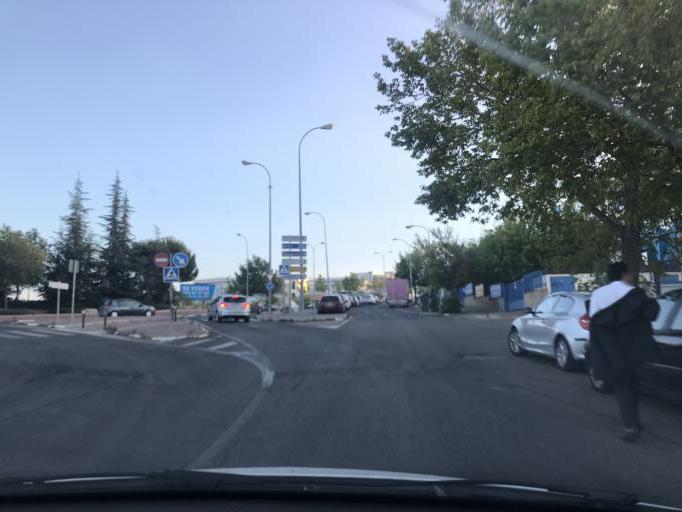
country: ES
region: Madrid
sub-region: Provincia de Madrid
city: Alcobendas
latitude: 40.5355
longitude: -3.6568
